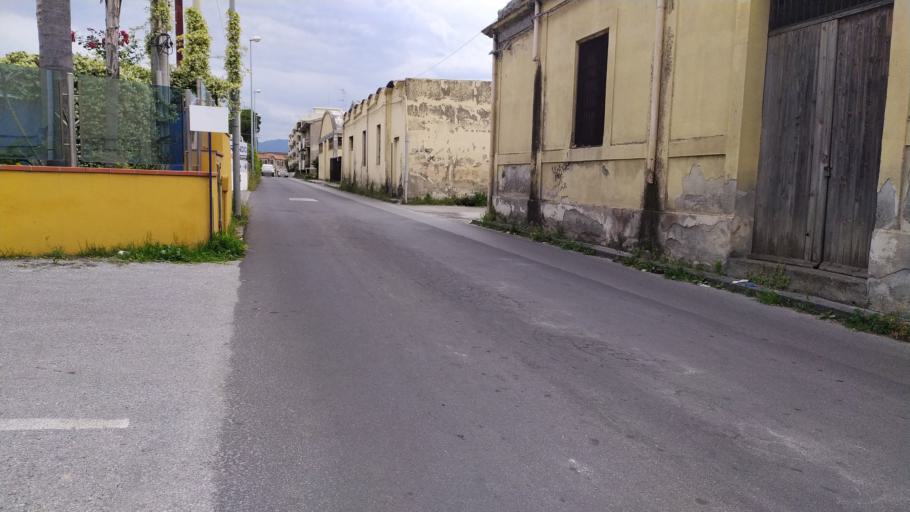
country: IT
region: Sicily
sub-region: Messina
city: Milazzo
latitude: 38.2126
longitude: 15.2419
